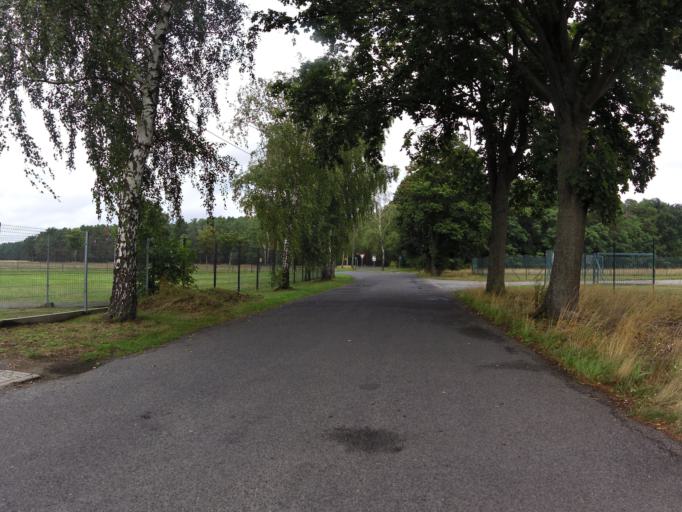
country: DE
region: Brandenburg
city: Storkow
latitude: 52.2712
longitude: 13.9433
